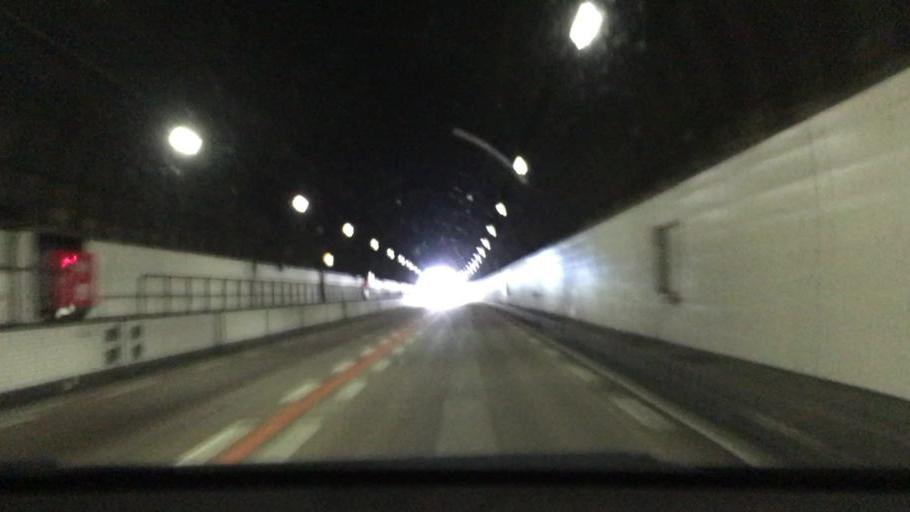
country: JP
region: Yamaguchi
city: Ogori-shimogo
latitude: 34.1254
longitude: 131.4542
